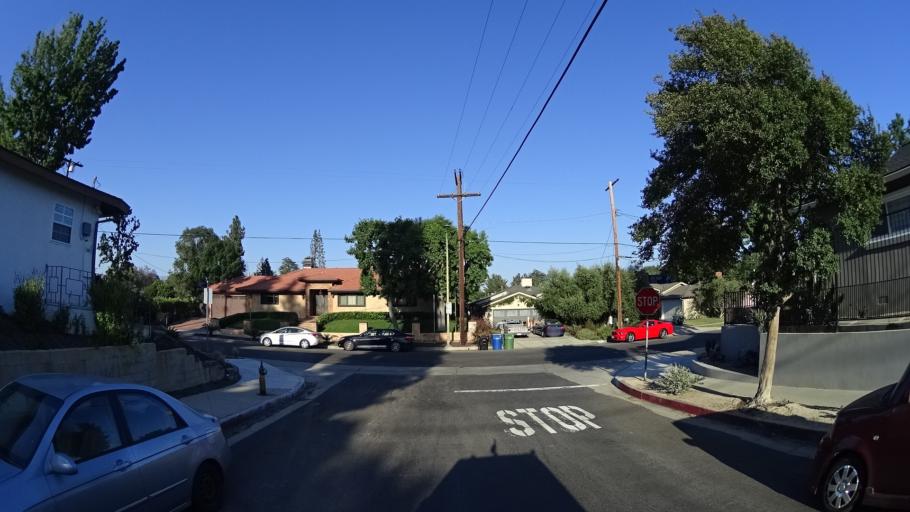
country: US
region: California
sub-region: Los Angeles County
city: North Hollywood
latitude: 34.1612
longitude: -118.4129
